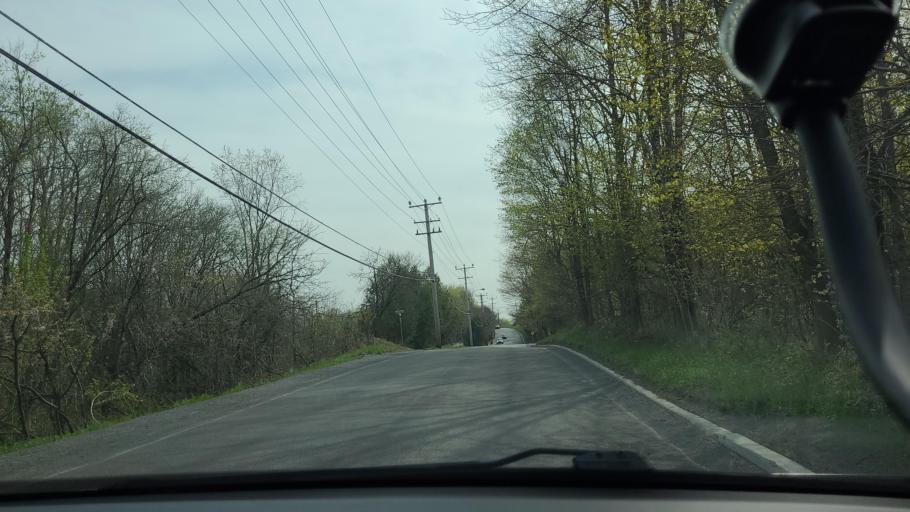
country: CA
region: Quebec
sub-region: Laurentides
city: Prevost
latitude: 45.8803
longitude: -74.0620
